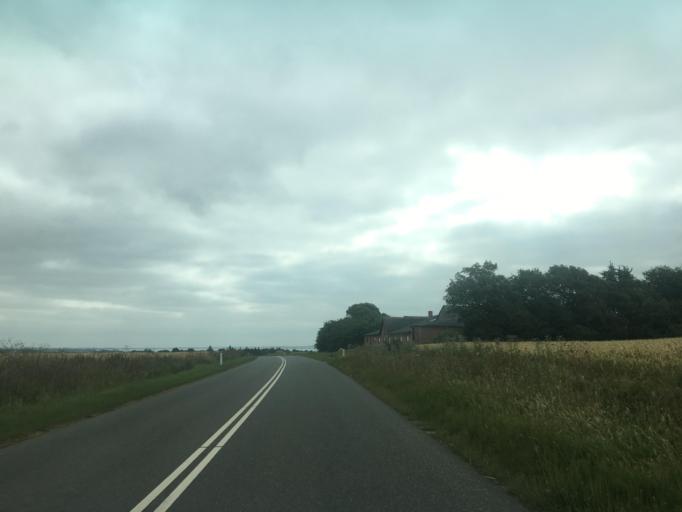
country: DK
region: North Denmark
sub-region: Thisted Kommune
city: Hurup
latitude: 56.8181
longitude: 8.4997
